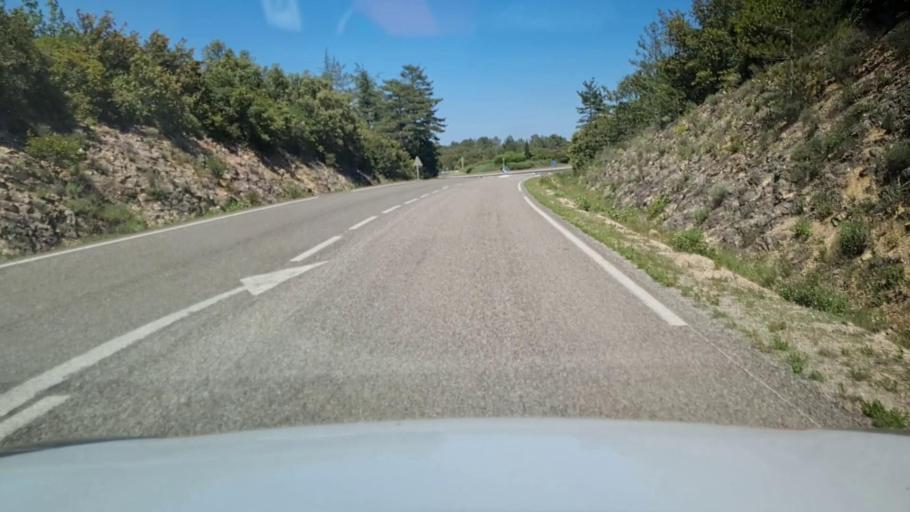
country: FR
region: Languedoc-Roussillon
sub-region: Departement du Gard
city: Clarensac
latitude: 43.8592
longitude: 4.2153
